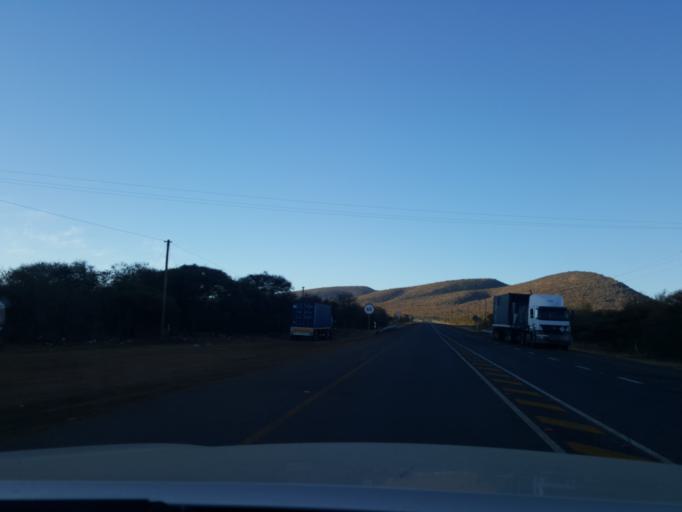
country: BW
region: South East
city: Lobatse
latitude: -25.2832
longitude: 25.7218
